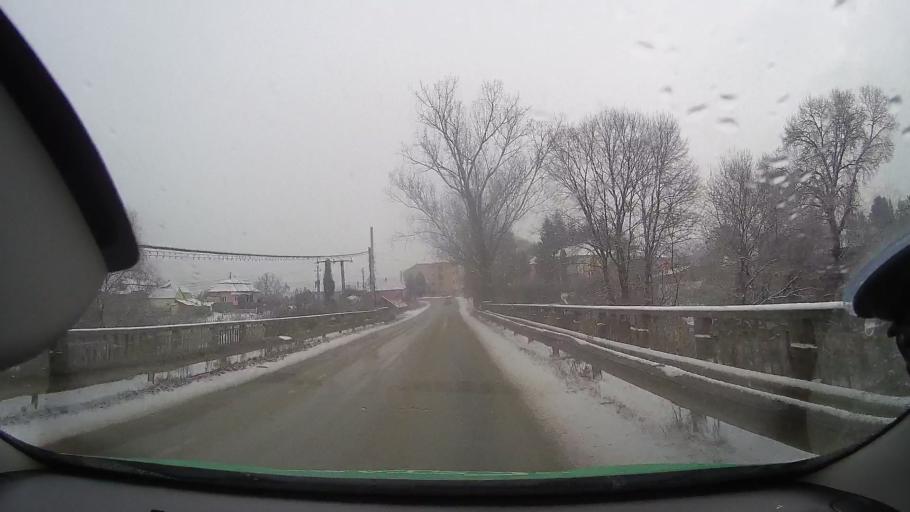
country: RO
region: Alba
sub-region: Municipiul Aiud
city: Ciumbrud
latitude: 46.3056
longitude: 23.7590
